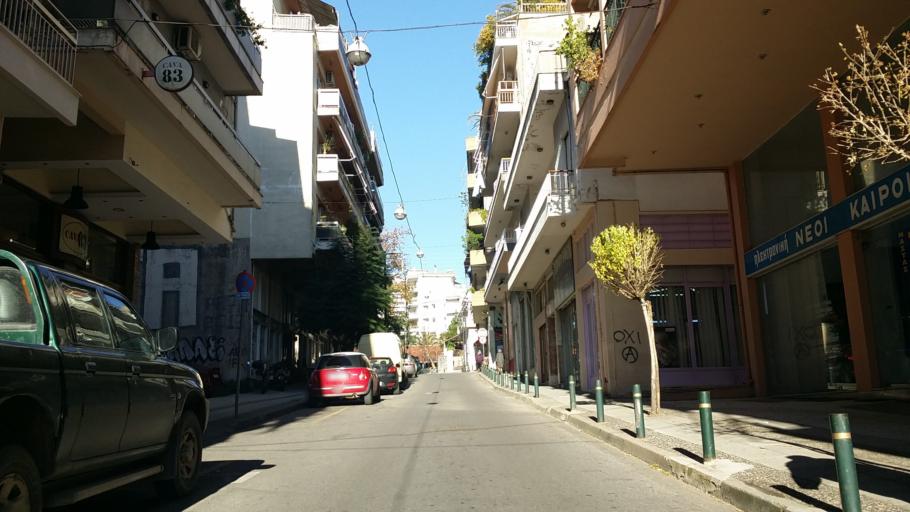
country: GR
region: West Greece
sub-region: Nomos Aitolias kai Akarnanias
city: Agrinio
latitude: 38.6263
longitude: 21.4125
